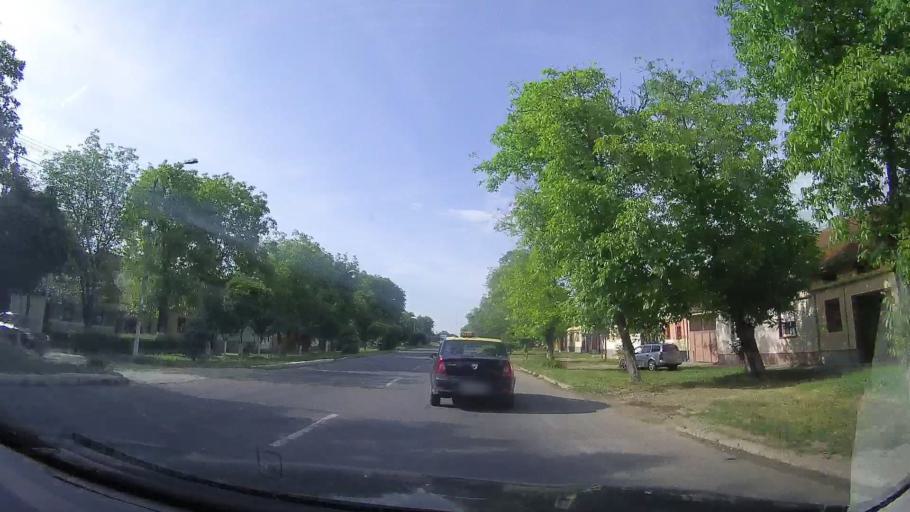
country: RO
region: Caras-Severin
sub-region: Municipiul Caransebes
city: Caransebes
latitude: 45.3950
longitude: 22.2265
